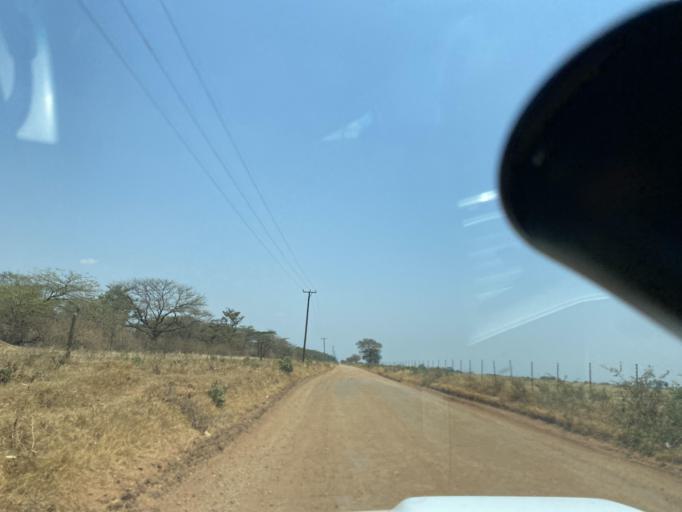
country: ZM
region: Lusaka
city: Lusaka
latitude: -15.4372
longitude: 28.0686
